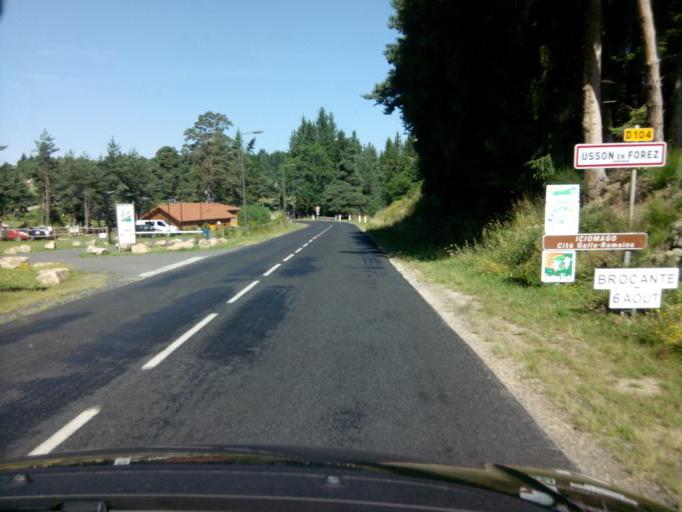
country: FR
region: Rhone-Alpes
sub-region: Departement de la Loire
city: Usson-en-Forez
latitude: 45.3922
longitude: 3.9564
